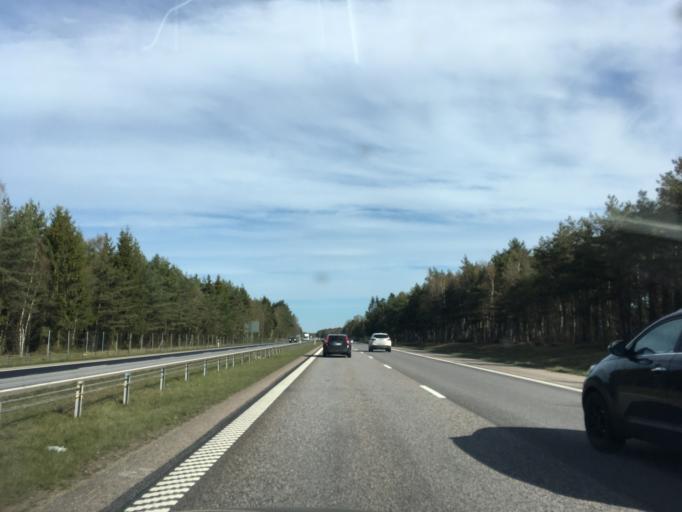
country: SE
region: Halland
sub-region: Laholms Kommun
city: Mellbystrand
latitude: 56.5515
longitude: 12.9637
